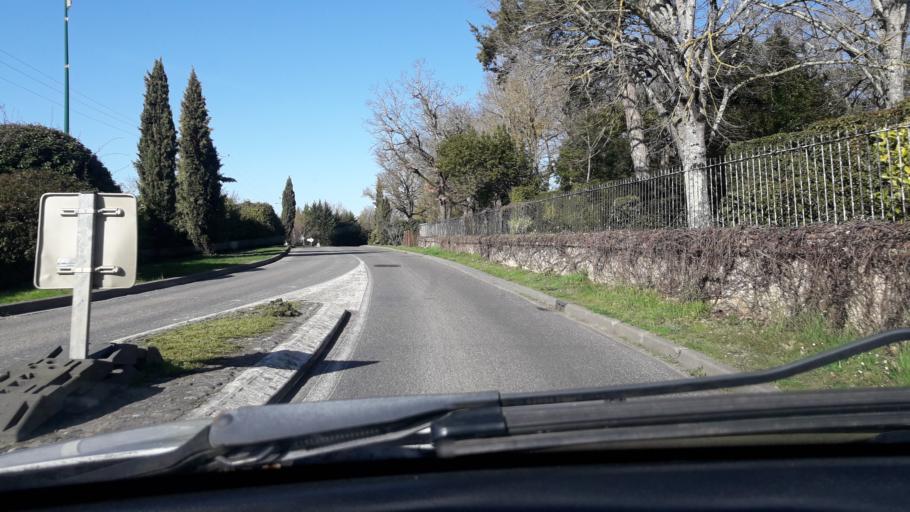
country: FR
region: Midi-Pyrenees
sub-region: Departement du Gers
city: Pujaudran
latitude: 43.6633
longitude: 1.0214
